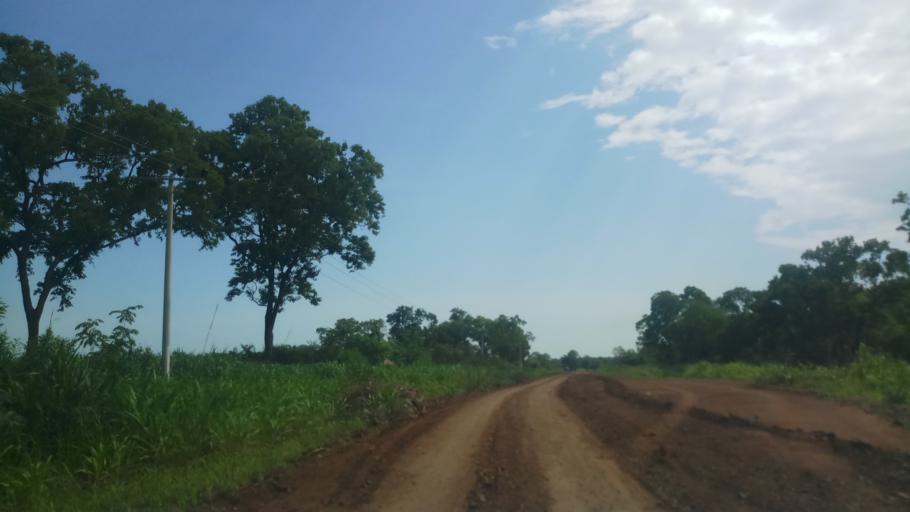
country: ET
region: Gambela
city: Gambela
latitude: 8.2064
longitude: 34.5134
